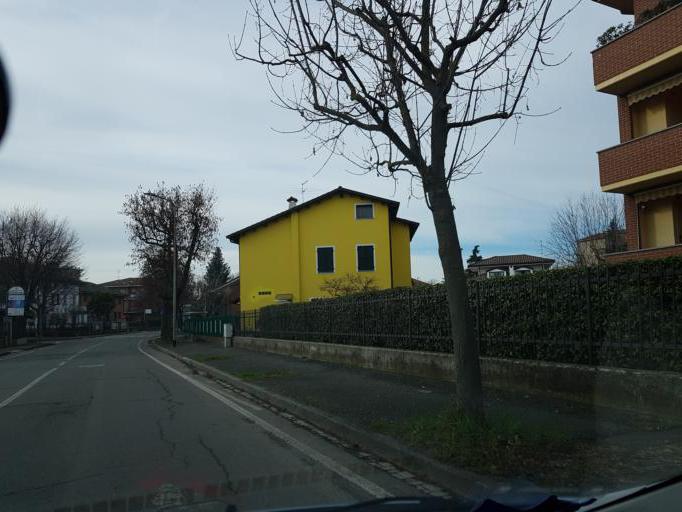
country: IT
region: Piedmont
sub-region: Provincia di Alessandria
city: Novi Ligure
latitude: 44.7613
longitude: 8.7998
